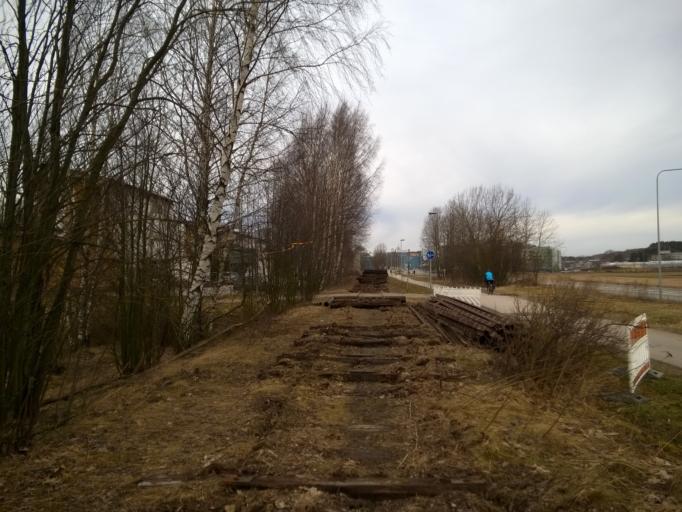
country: FI
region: Uusimaa
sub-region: Helsinki
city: Vantaa
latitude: 60.2229
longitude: 25.0253
